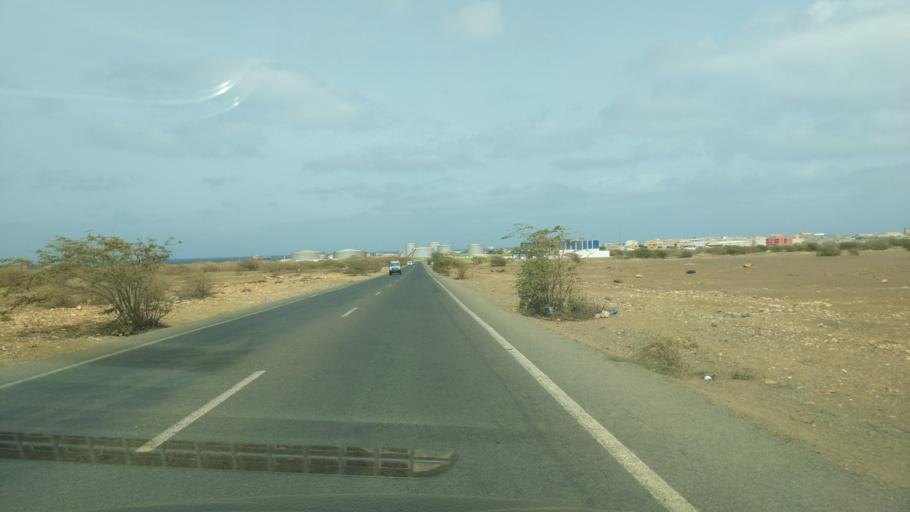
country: CV
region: Sal
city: Espargos
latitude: 16.7590
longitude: -22.9702
